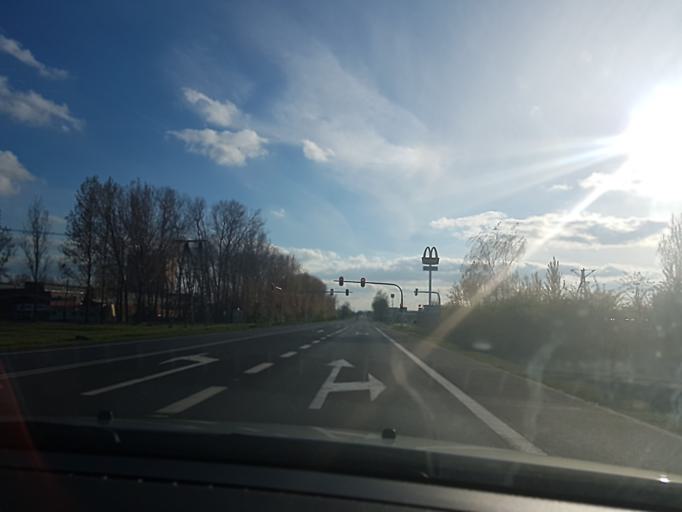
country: PL
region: Lodz Voivodeship
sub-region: Powiat kutnowski
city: Kutno
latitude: 52.2205
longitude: 19.3940
